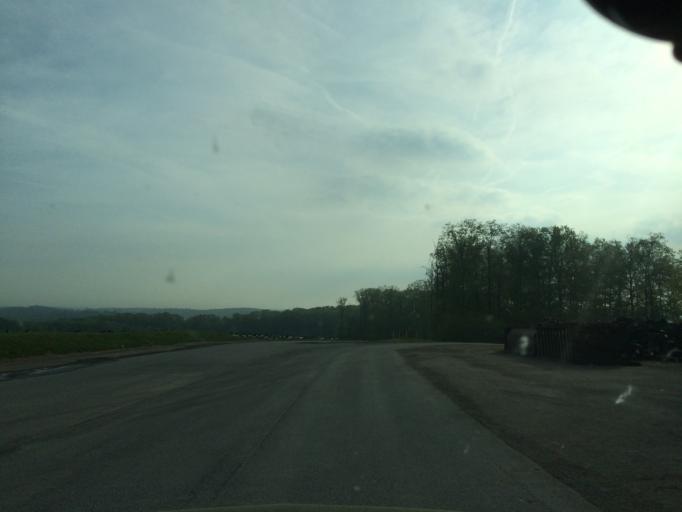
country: US
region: Maryland
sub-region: Carroll County
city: Westminster
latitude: 39.5514
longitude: -76.9415
